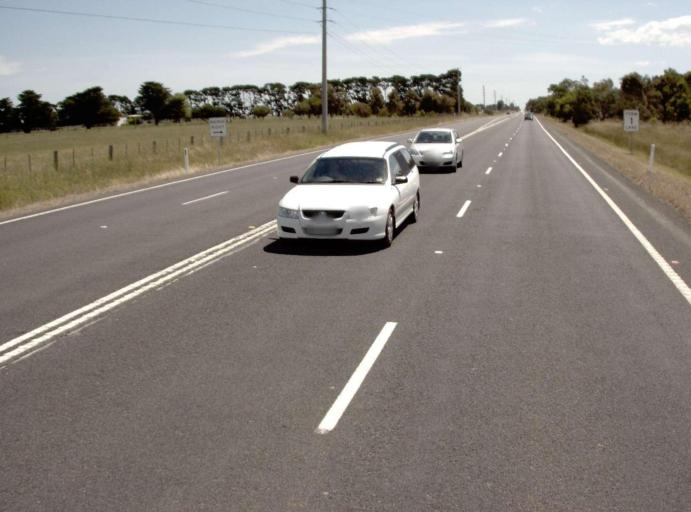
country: AU
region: Victoria
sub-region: Wellington
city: Sale
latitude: -38.1037
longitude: 146.9278
